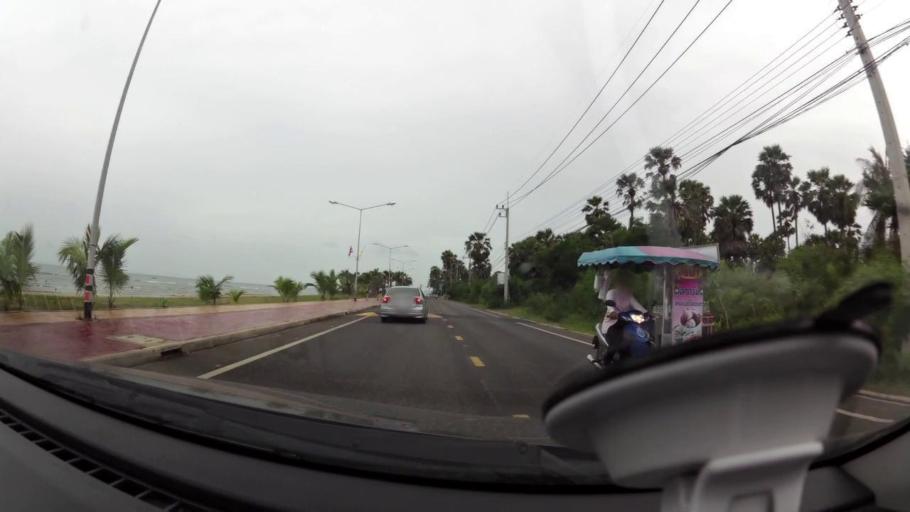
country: TH
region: Prachuap Khiri Khan
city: Pran Buri
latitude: 12.3800
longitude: 99.9999
